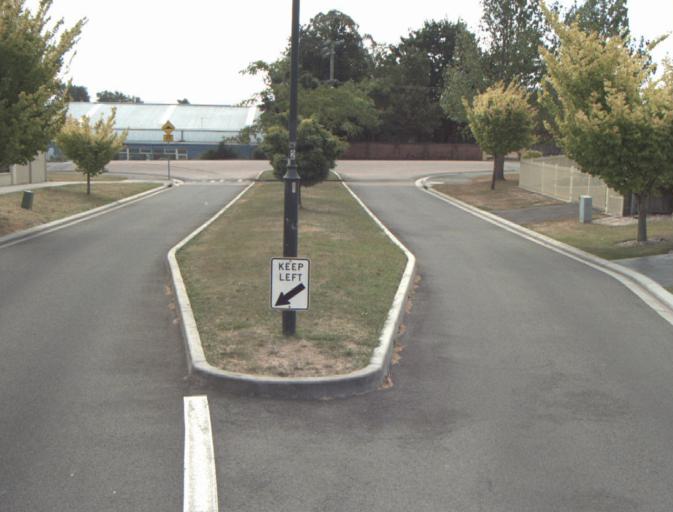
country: AU
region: Tasmania
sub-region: Launceston
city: East Launceston
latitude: -41.4330
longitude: 147.1568
